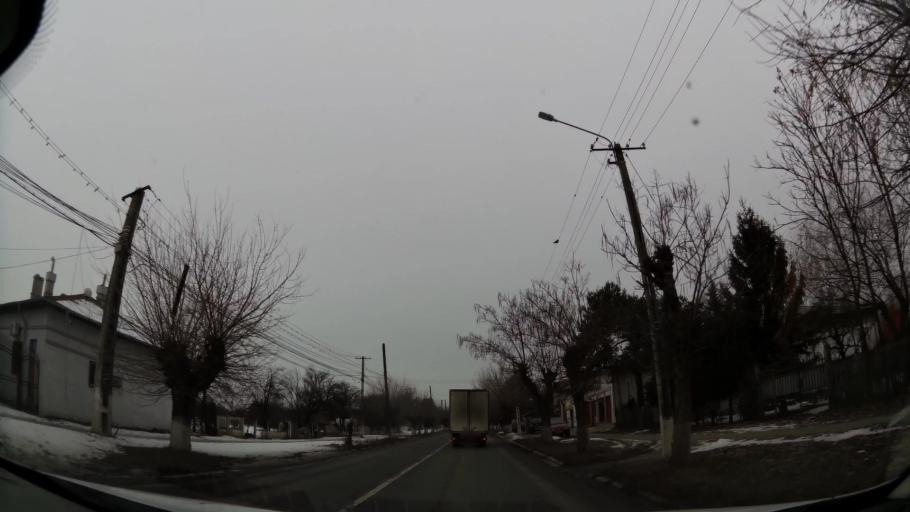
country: RO
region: Dambovita
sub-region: Comuna Racari
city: Racari
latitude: 44.6236
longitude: 25.7483
